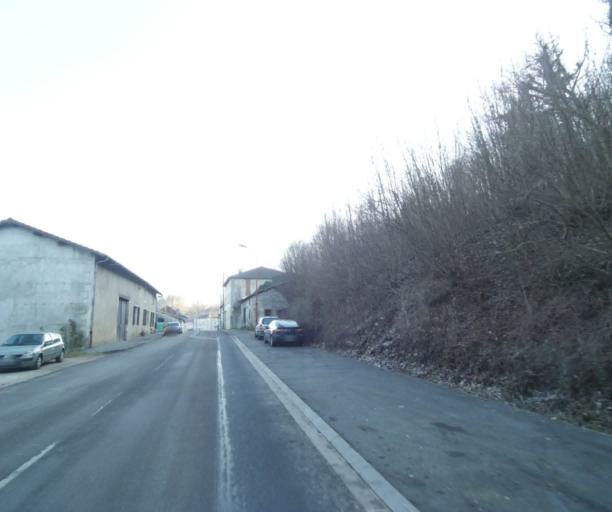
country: FR
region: Champagne-Ardenne
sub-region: Departement de la Haute-Marne
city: Bienville
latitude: 48.5503
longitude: 5.0707
